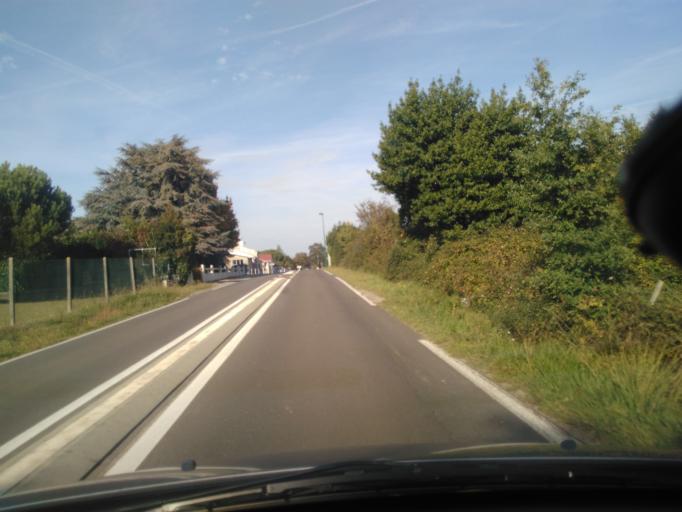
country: FR
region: Pays de la Loire
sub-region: Departement de la Vendee
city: Grosbreuil
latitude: 46.5239
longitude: -1.5529
